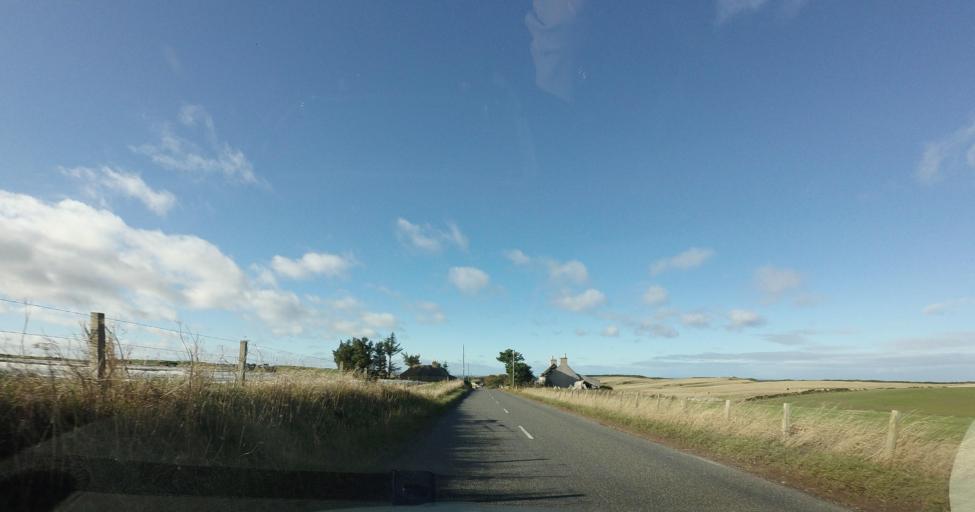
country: GB
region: Scotland
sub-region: Aberdeenshire
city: Macduff
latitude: 57.6636
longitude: -2.3811
